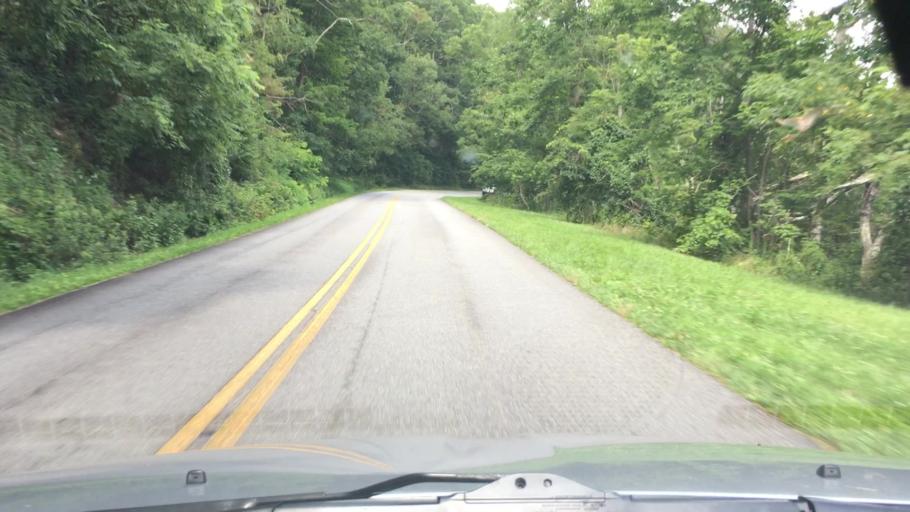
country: US
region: North Carolina
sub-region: Buncombe County
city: Weaverville
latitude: 35.6621
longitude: -82.4795
